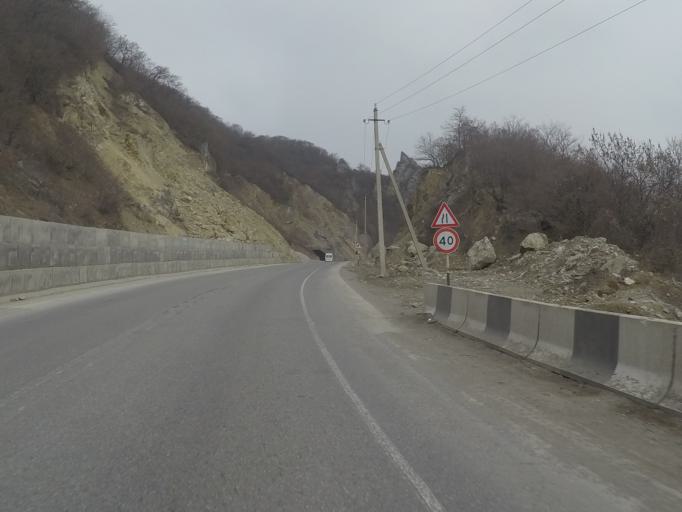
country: GE
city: Zhinvali
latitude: 42.1381
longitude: 44.7691
